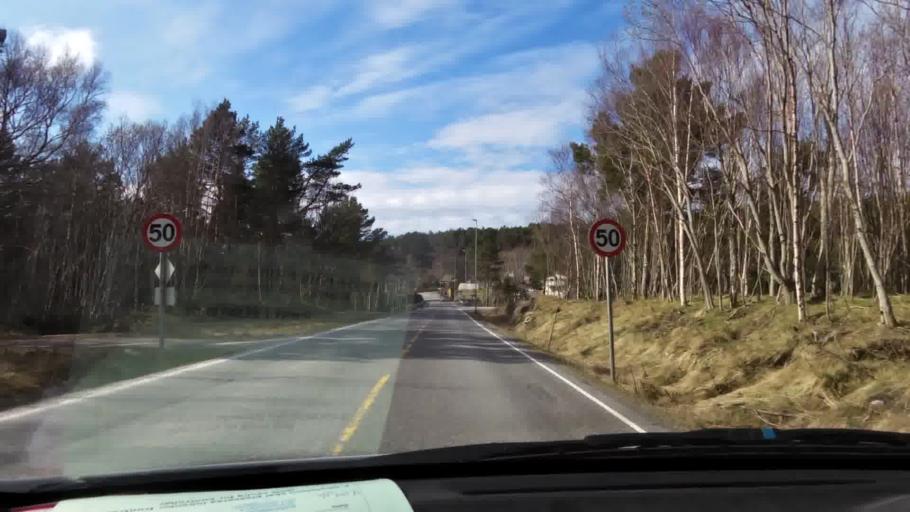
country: NO
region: More og Romsdal
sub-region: Kristiansund
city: Rensvik
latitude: 63.1075
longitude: 7.8233
